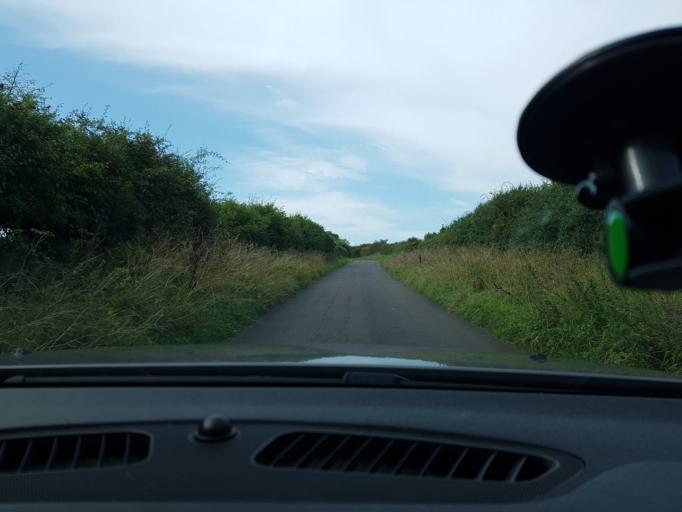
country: GB
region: England
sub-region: West Berkshire
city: Hungerford
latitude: 51.4124
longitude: -1.5295
